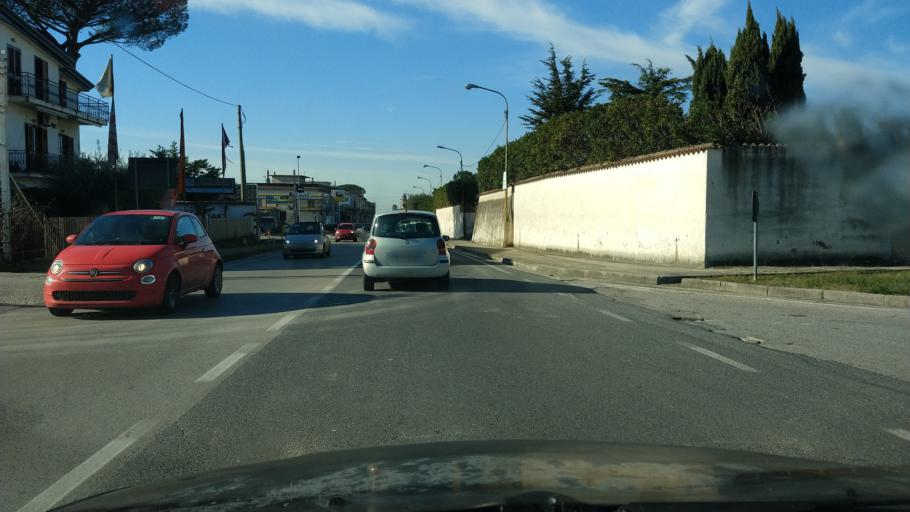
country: IT
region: Campania
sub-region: Provincia di Avellino
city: Avella
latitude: 40.9524
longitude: 14.5945
